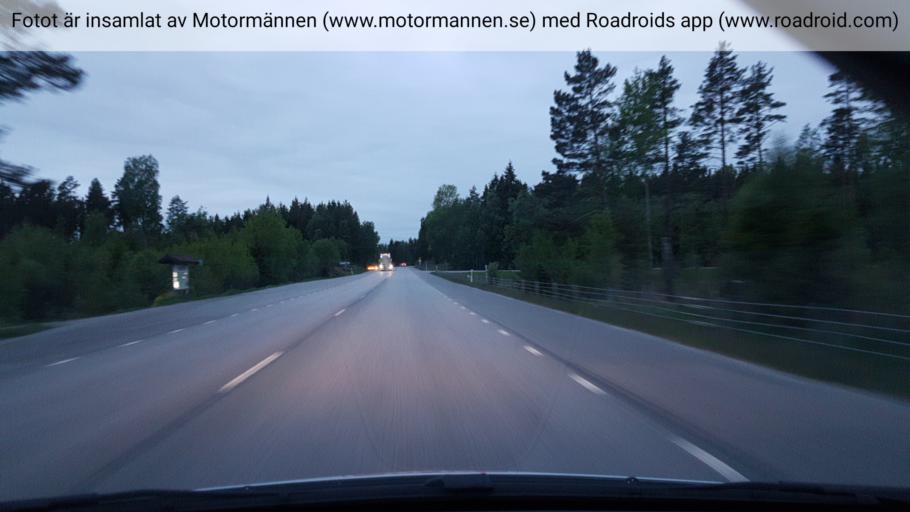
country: SE
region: Uppsala
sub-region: Heby Kommun
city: Heby
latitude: 59.9398
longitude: 16.7643
